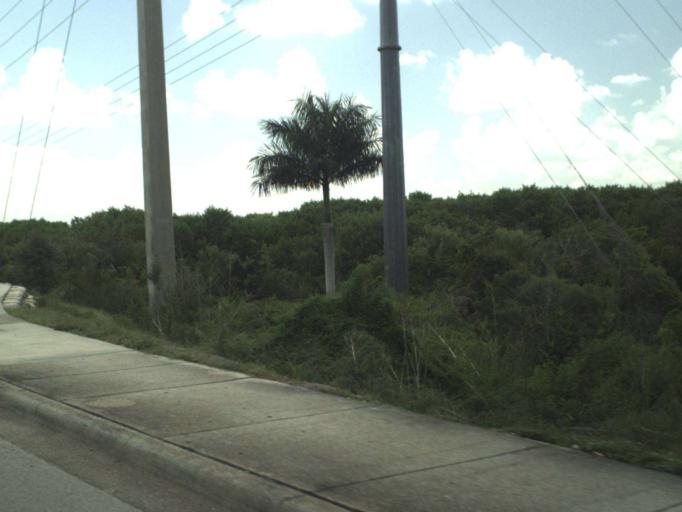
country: US
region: Florida
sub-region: Saint Lucie County
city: Port Saint Lucie
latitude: 27.2719
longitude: -80.3202
